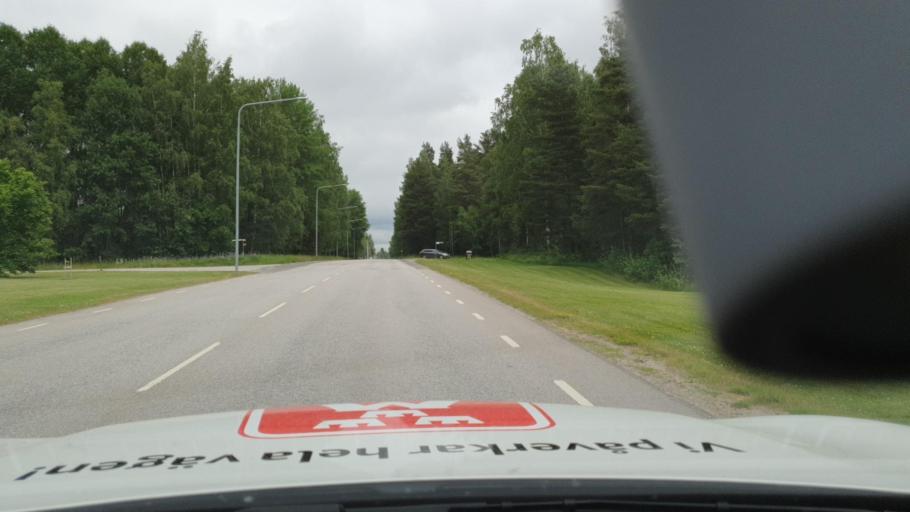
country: SE
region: Vaestra Goetaland
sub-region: Tibro Kommun
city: Tibro
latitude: 58.4073
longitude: 14.1517
